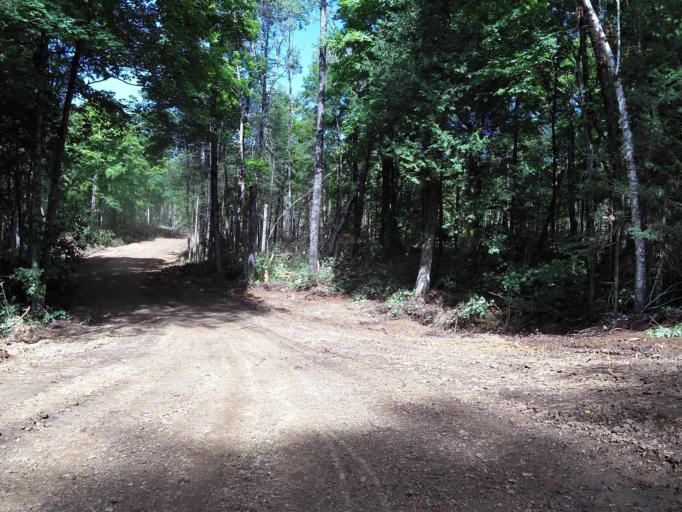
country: CA
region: Ontario
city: Renfrew
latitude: 45.1066
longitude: -76.7169
